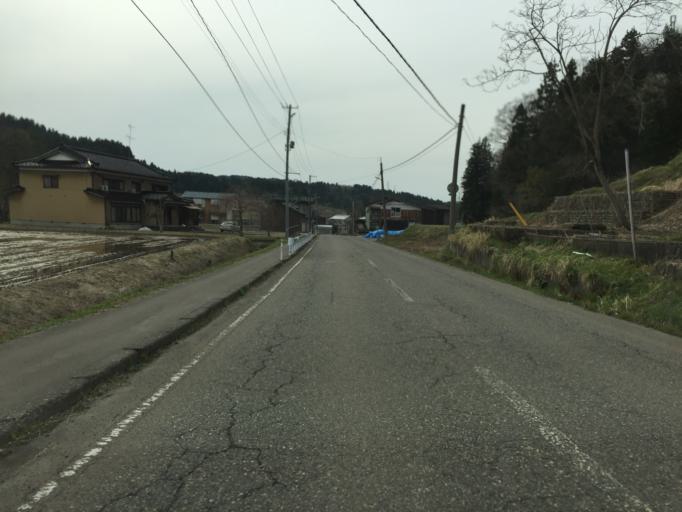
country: JP
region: Niigata
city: Tochio-honcho
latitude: 37.4482
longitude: 139.0182
